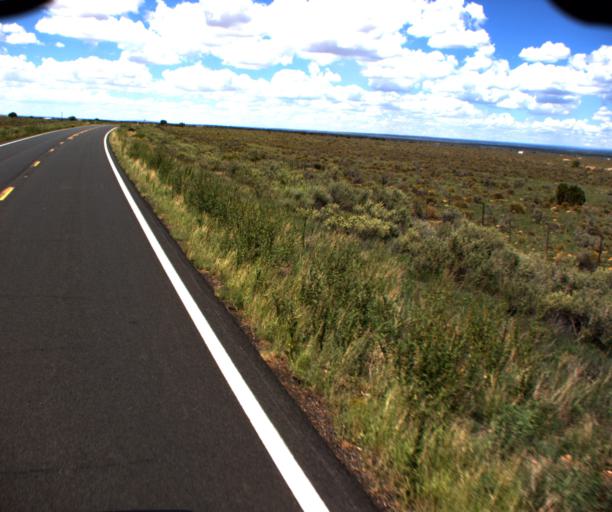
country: US
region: Arizona
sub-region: Coconino County
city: Williams
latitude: 35.6254
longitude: -112.1124
